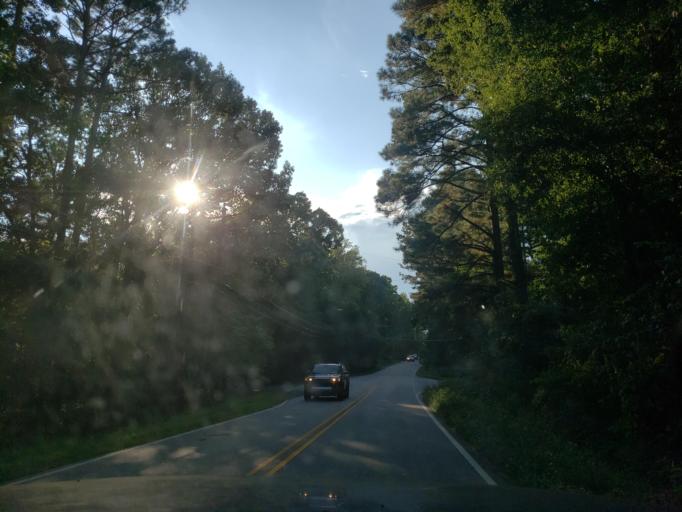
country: US
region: North Carolina
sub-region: Durham County
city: Durham
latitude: 35.9794
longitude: -78.9481
